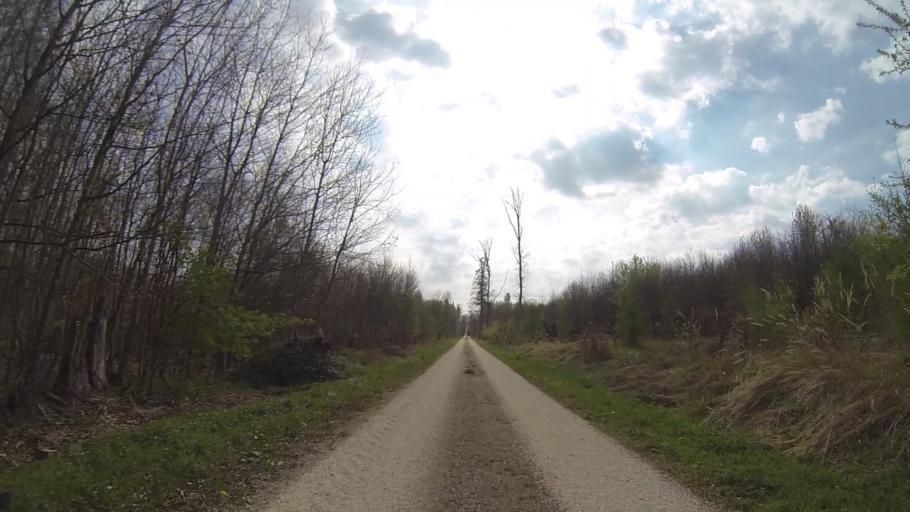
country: DE
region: Baden-Wuerttemberg
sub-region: Regierungsbezirk Stuttgart
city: Heidenheim an der Brenz
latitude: 48.6862
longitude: 10.1975
